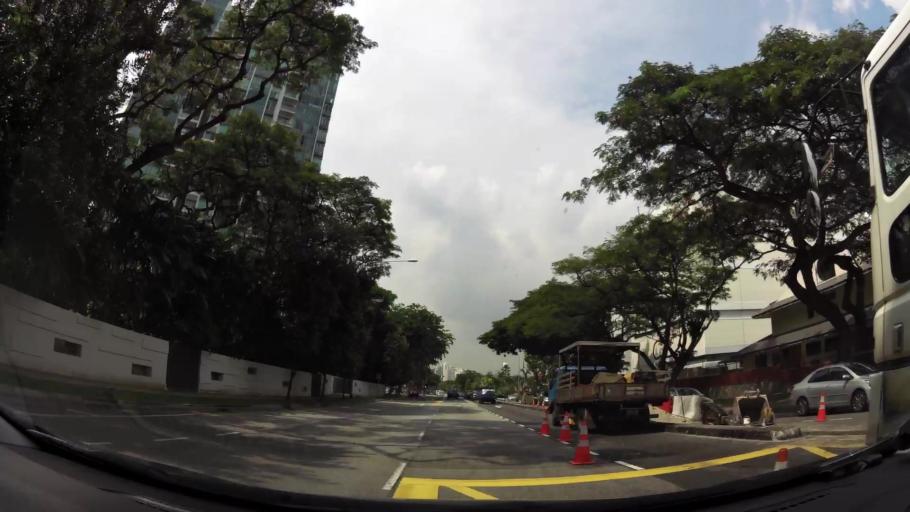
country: SG
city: Singapore
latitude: 1.3022
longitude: 103.8980
